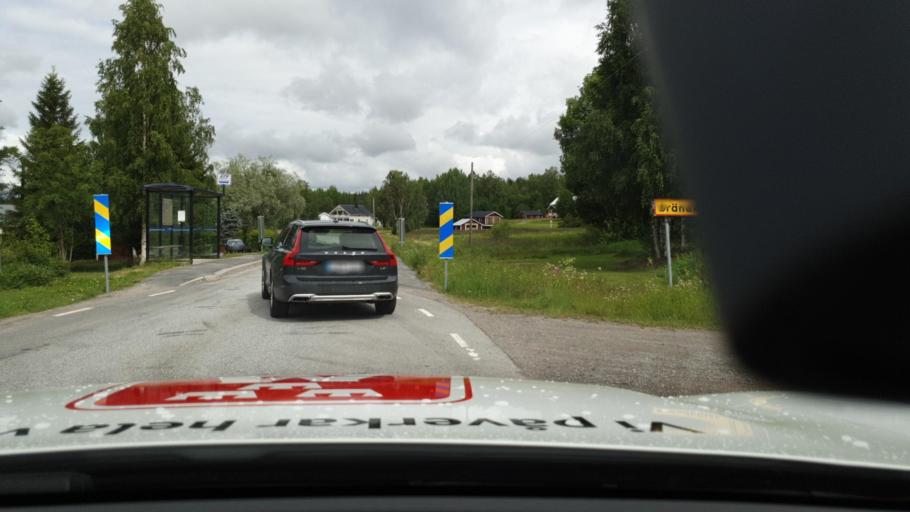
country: SE
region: Norrbotten
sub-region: Pitea Kommun
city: Rosvik
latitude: 65.5832
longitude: 21.7747
